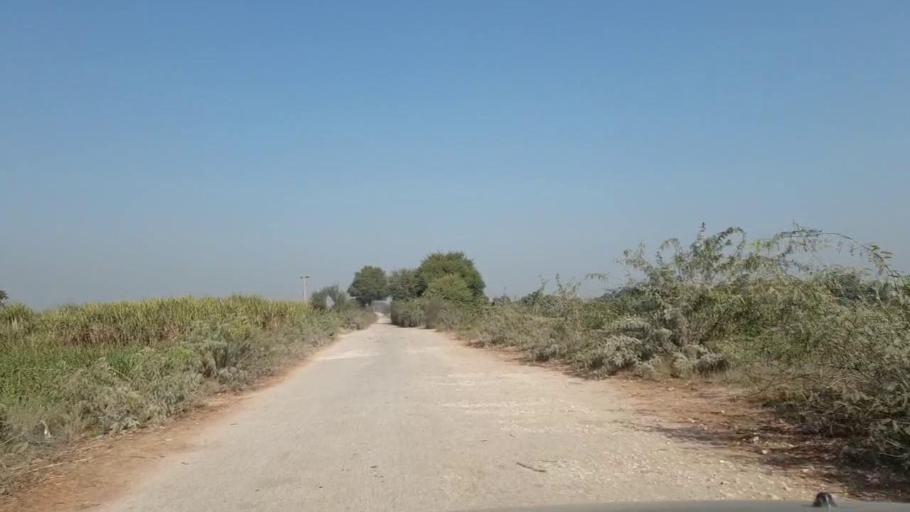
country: PK
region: Sindh
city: Tando Allahyar
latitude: 25.5670
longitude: 68.6080
